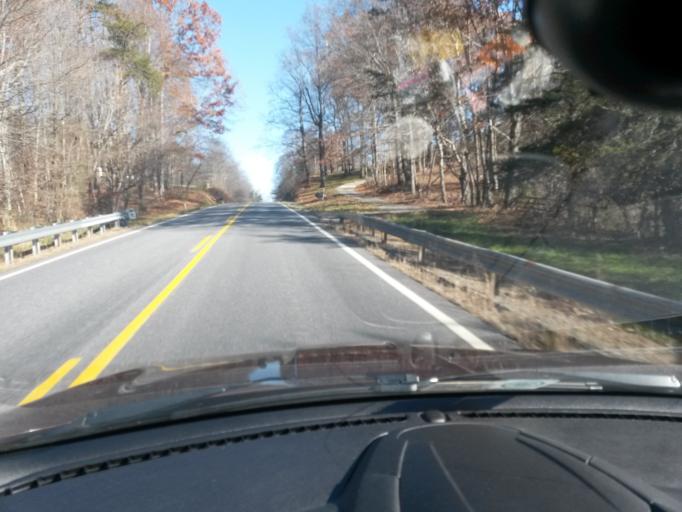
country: US
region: Virginia
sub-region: Patrick County
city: Patrick Springs
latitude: 36.7618
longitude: -80.1770
